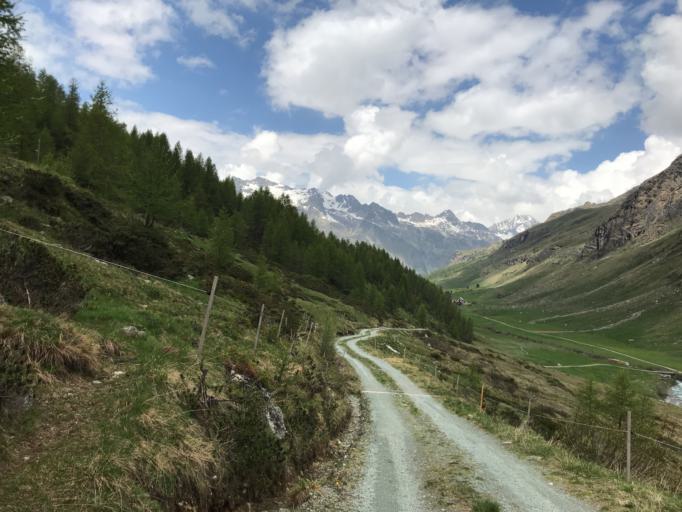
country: CH
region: Grisons
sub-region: Maloja District
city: Silvaplana
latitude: 46.3868
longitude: 9.7813
